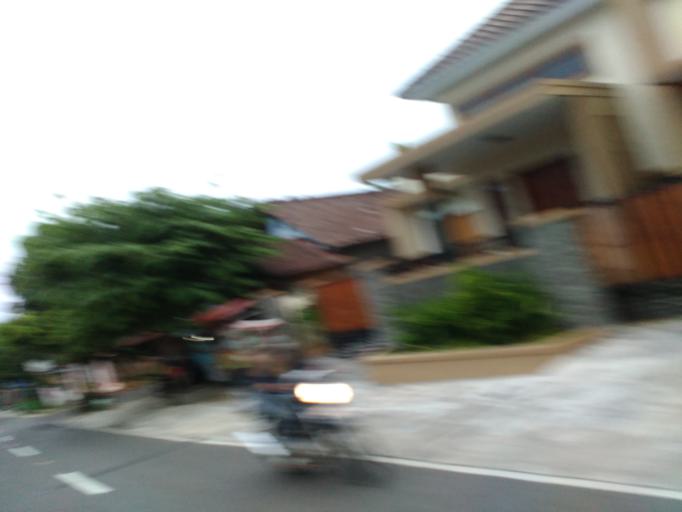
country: ID
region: Central Java
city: Boyolali
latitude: -7.5356
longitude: 110.6053
